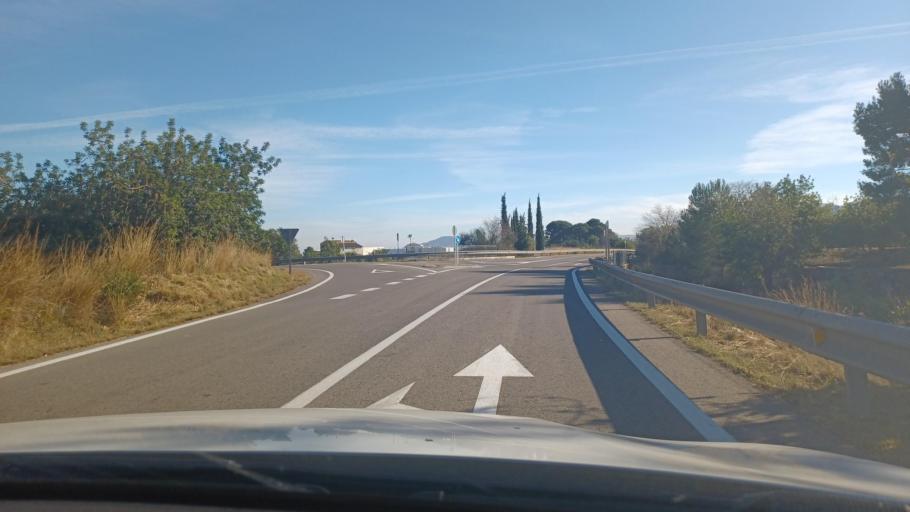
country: ES
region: Catalonia
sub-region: Provincia de Tarragona
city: Santa Barbara
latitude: 40.7141
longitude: 0.4831
